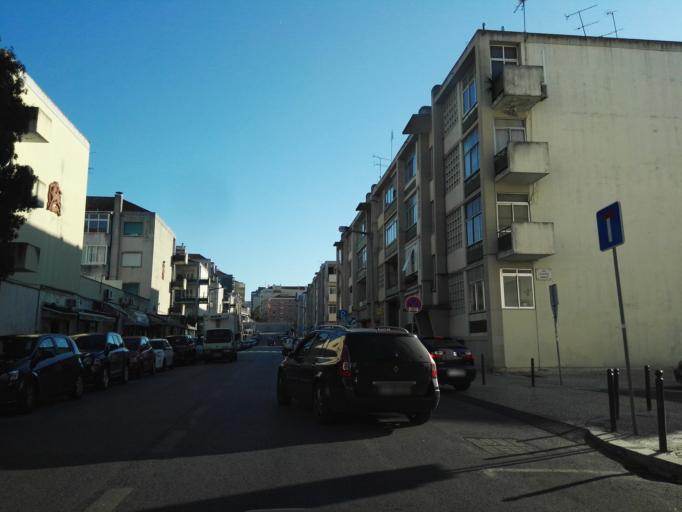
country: PT
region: Lisbon
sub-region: Lisbon
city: Lisbon
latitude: 38.7483
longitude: -9.1325
